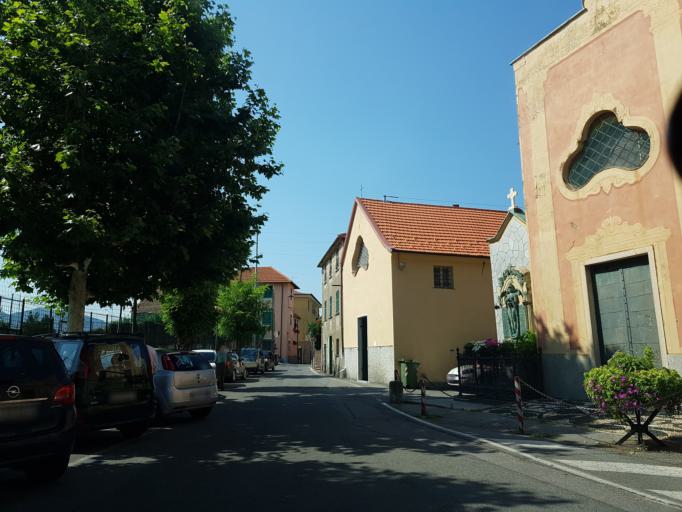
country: IT
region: Liguria
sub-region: Provincia di Genova
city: Pedemonte
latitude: 44.4980
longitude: 8.9126
